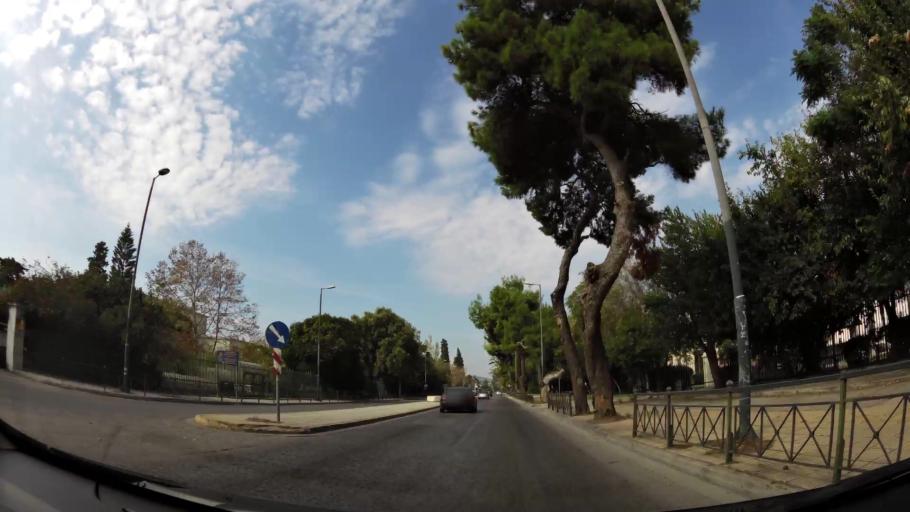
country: GR
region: Attica
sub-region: Nomarchia Athinas
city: Athens
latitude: 37.9836
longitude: 23.7048
